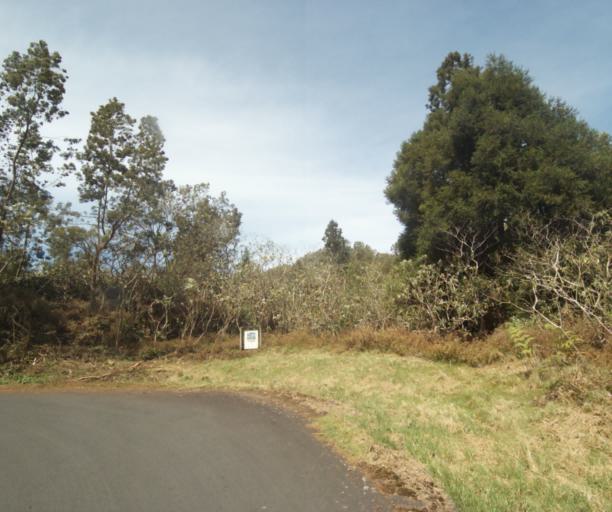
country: RE
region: Reunion
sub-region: Reunion
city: Trois-Bassins
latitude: -21.0535
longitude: 55.3547
